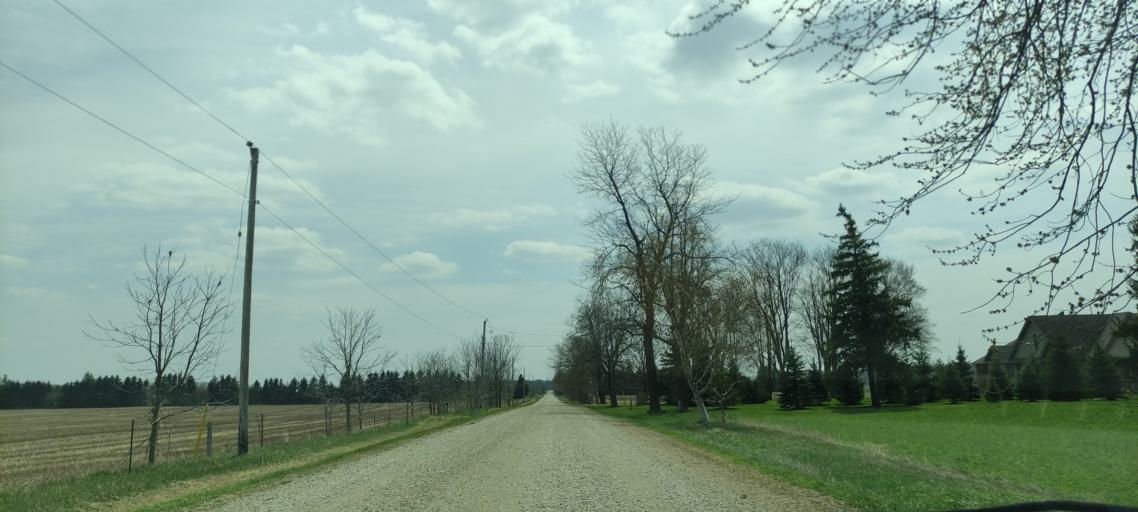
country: CA
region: Ontario
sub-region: Oxford County
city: Woodstock
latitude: 43.3416
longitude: -80.7411
